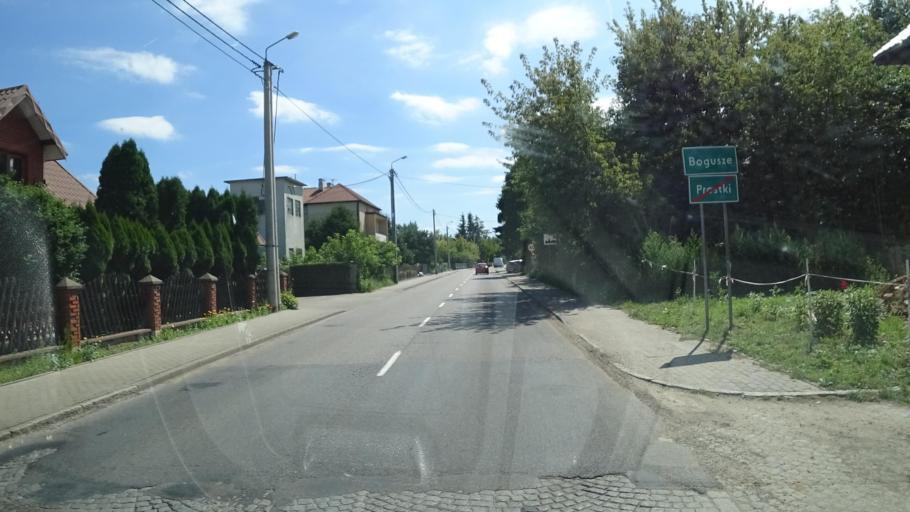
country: PL
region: Warmian-Masurian Voivodeship
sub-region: Powiat elcki
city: Prostki
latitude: 53.6903
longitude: 22.4469
